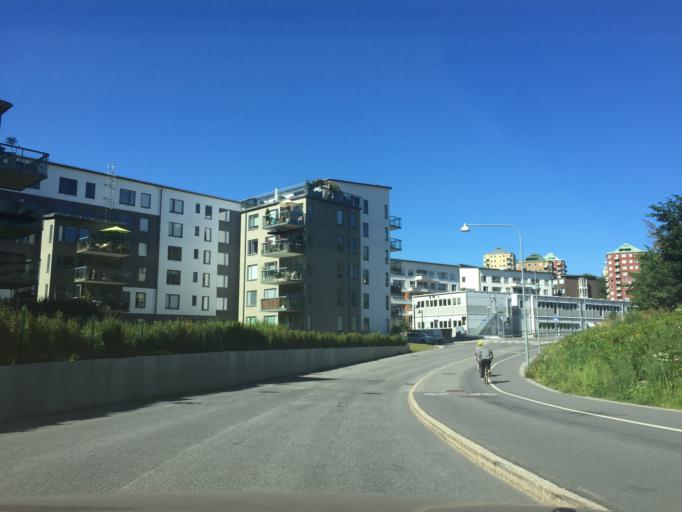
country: SE
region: Stockholm
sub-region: Stockholms Kommun
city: OEstermalm
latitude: 59.3092
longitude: 18.1051
